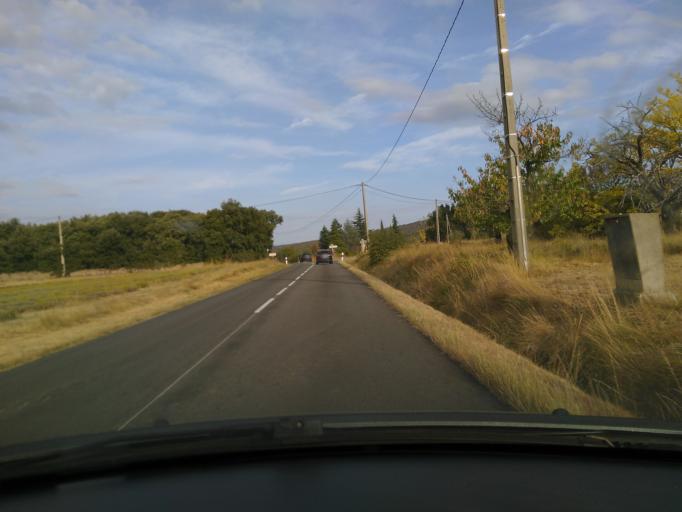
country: FR
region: Rhone-Alpes
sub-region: Departement de la Drome
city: Taulignan
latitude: 44.4337
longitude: 5.0229
